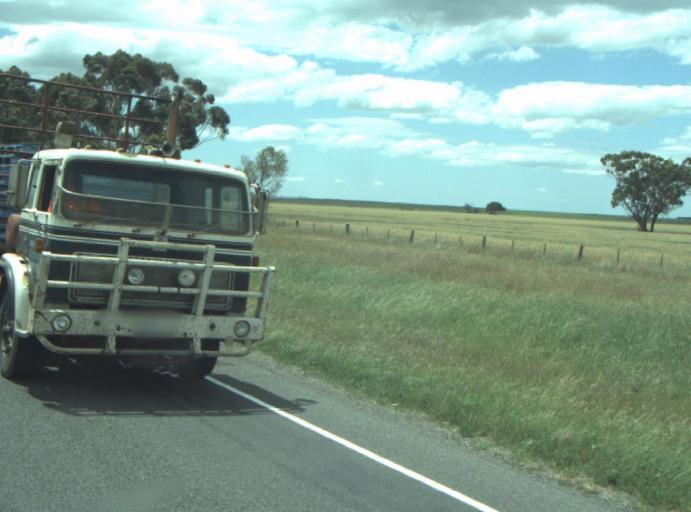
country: AU
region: Victoria
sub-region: Greater Geelong
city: Lara
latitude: -37.8793
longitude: 144.3798
